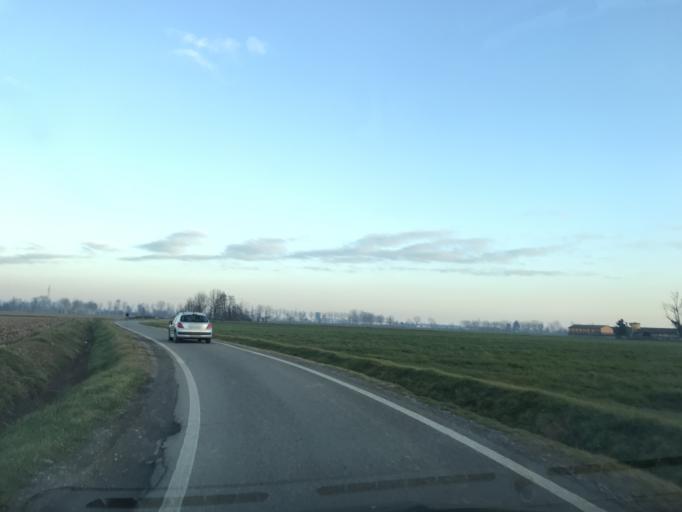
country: IT
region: Lombardy
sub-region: Provincia di Lodi
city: Muzza di Cornegliano Laudense
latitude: 45.2765
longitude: 9.4784
